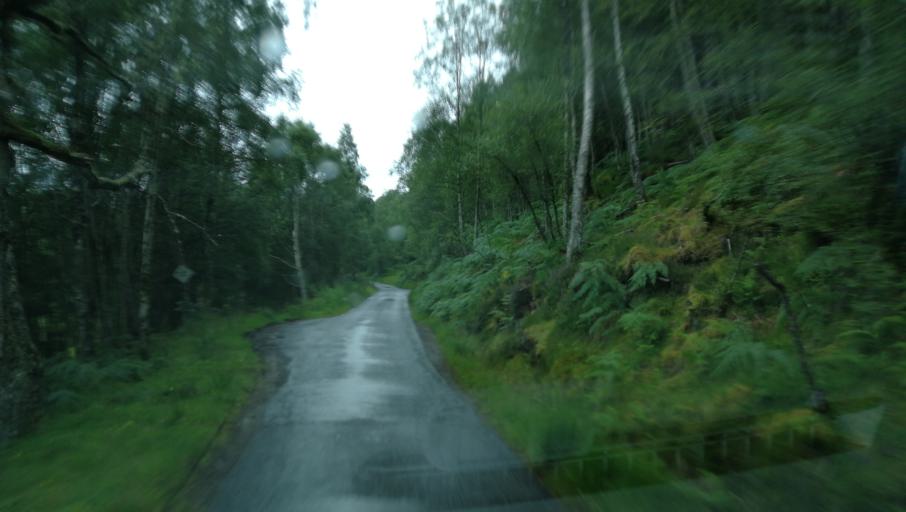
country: GB
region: Scotland
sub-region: Highland
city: Spean Bridge
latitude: 57.2783
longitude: -4.9421
